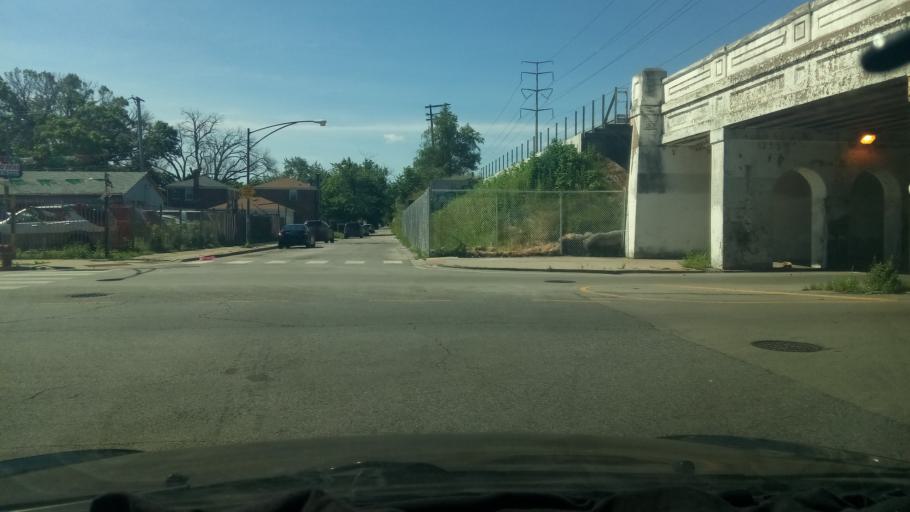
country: US
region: Illinois
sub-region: Cook County
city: Hometown
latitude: 41.7792
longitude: -87.7123
